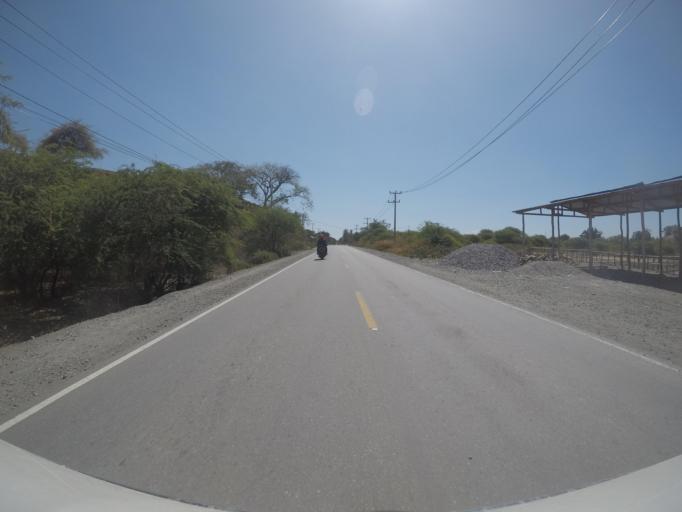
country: TL
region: Liquica
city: Liquica
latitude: -8.5667
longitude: 125.4261
